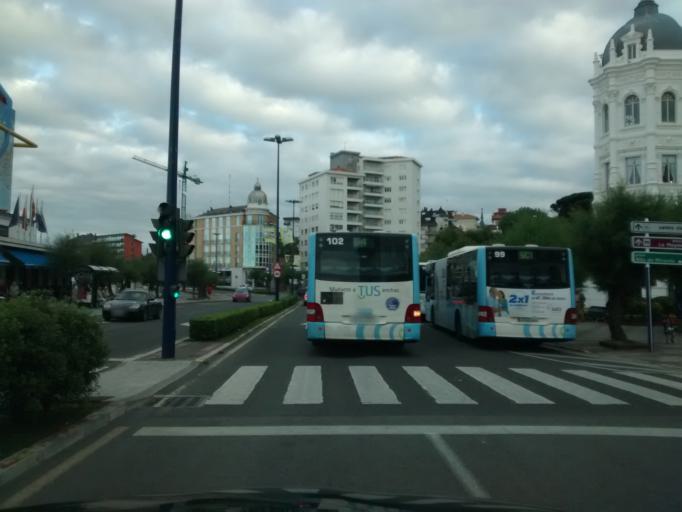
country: ES
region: Cantabria
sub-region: Provincia de Cantabria
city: Santander
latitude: 43.4724
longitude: -3.7825
